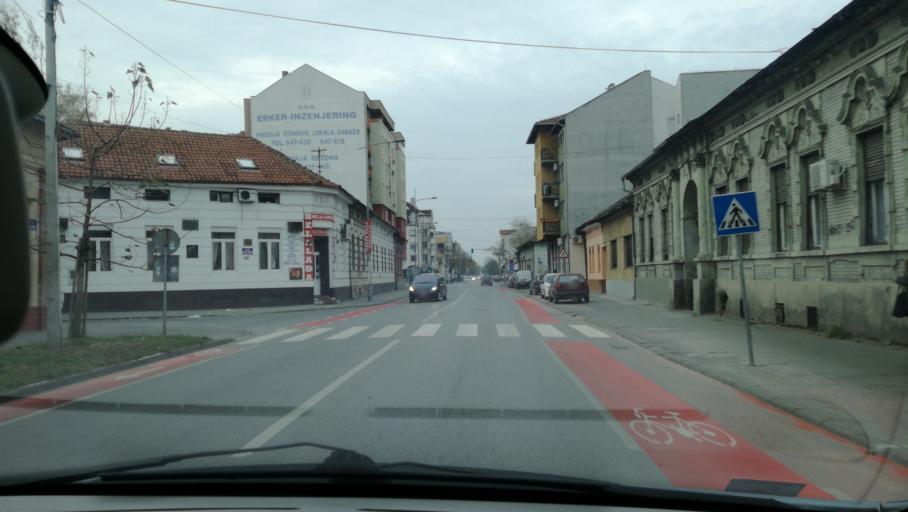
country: RS
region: Autonomna Pokrajina Vojvodina
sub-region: Juznobacki Okrug
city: Novi Sad
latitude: 45.2618
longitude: 19.8409
